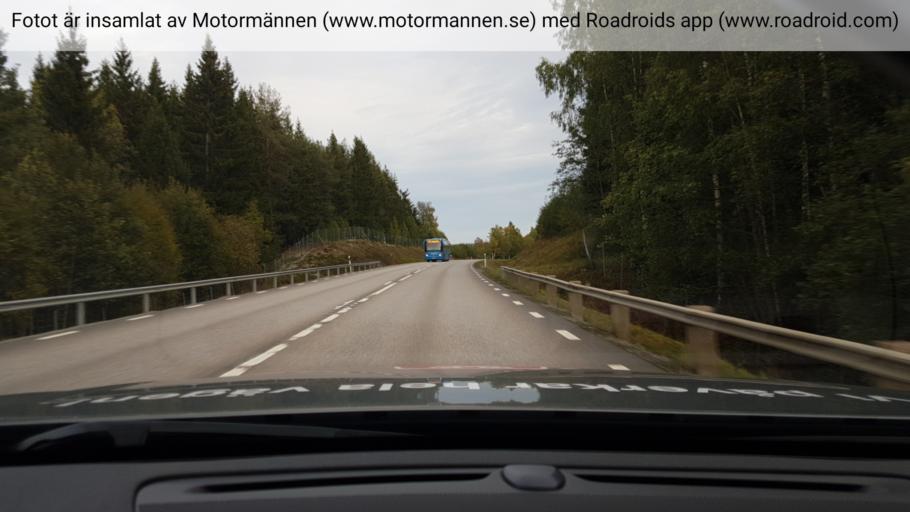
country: SE
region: Vaestra Goetaland
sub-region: Bengtsfors Kommun
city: Billingsfors
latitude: 59.0274
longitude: 12.3517
